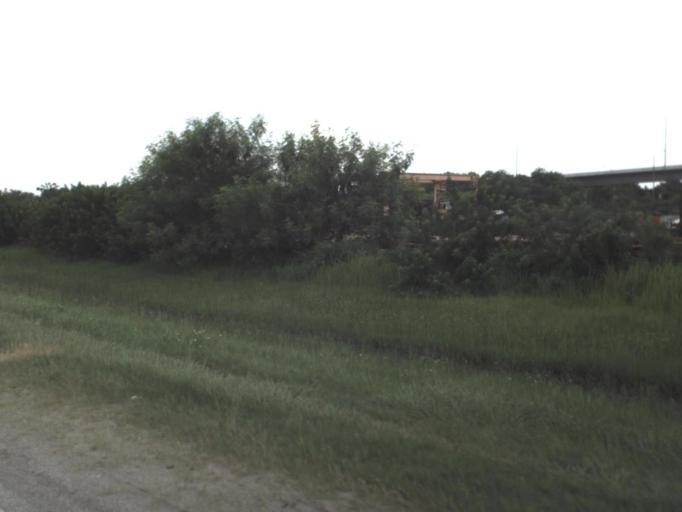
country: US
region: Florida
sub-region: Hillsborough County
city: Palm River-Clair Mel
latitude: 27.9520
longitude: -82.3958
